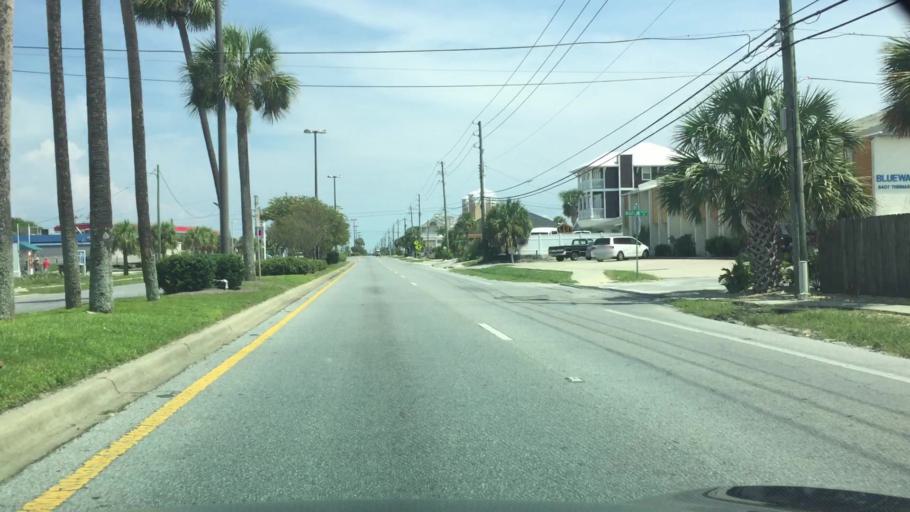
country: US
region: Florida
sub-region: Bay County
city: Panama City Beach
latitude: 30.1653
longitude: -85.7857
